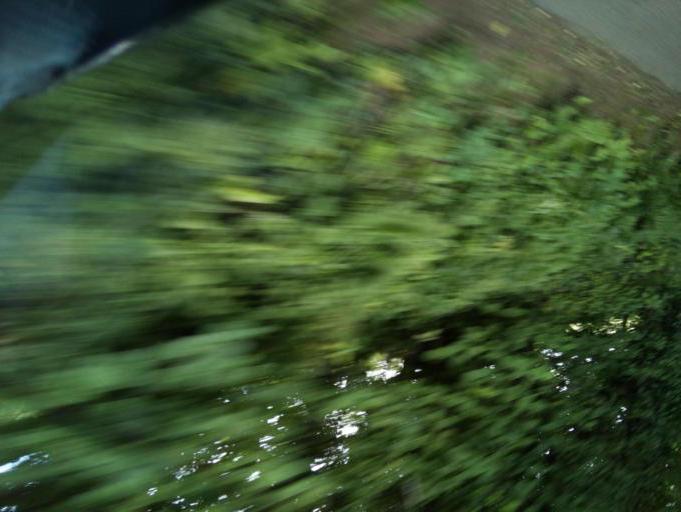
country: GB
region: England
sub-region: Devon
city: South Brent
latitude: 50.4032
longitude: -3.8239
